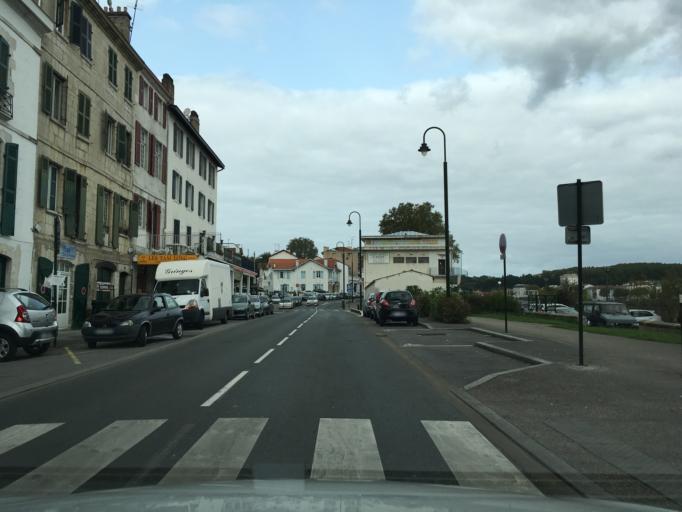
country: FR
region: Aquitaine
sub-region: Departement des Pyrenees-Atlantiques
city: Bayonne
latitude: 43.4887
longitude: -1.4656
